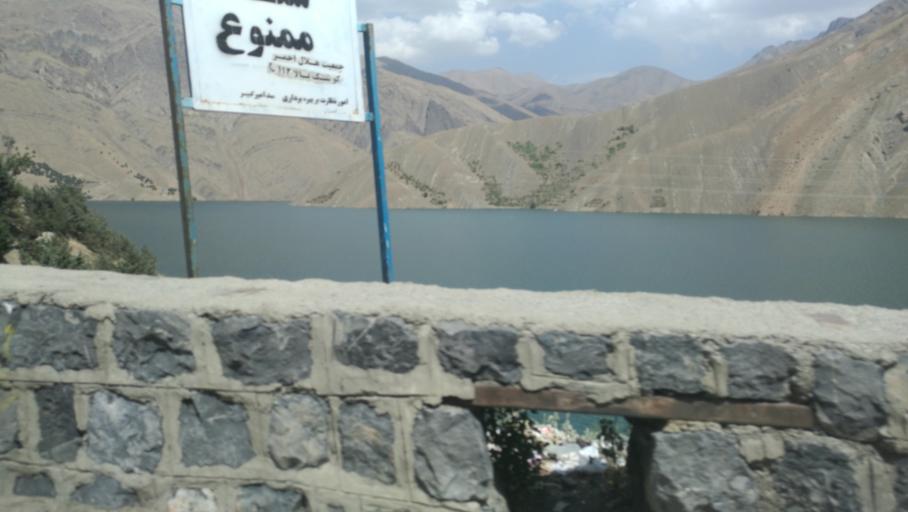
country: IR
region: Alborz
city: Karaj
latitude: 35.9650
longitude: 51.0931
